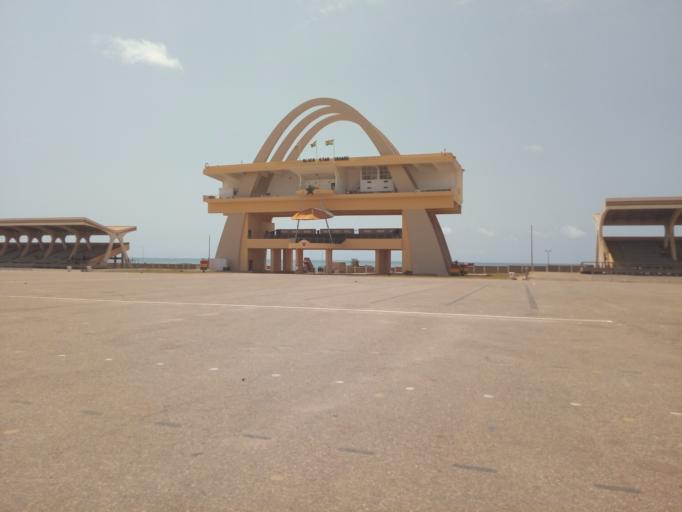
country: GH
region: Greater Accra
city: Accra
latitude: 5.5474
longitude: -0.1929
